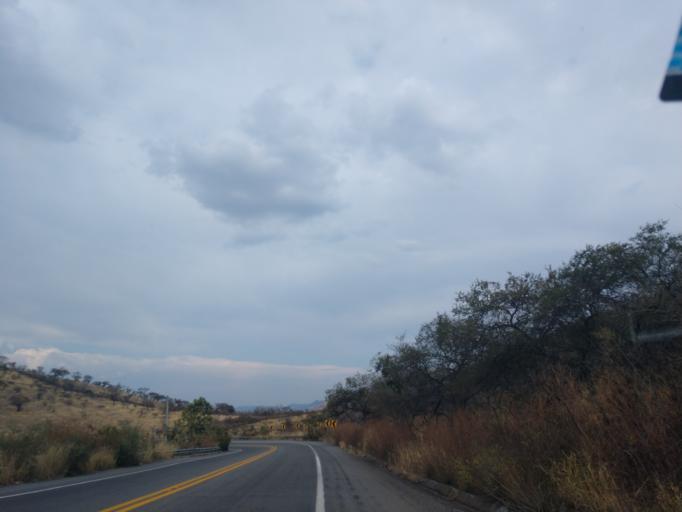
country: MX
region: Jalisco
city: La Manzanilla de la Paz
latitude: 20.1057
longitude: -103.1637
